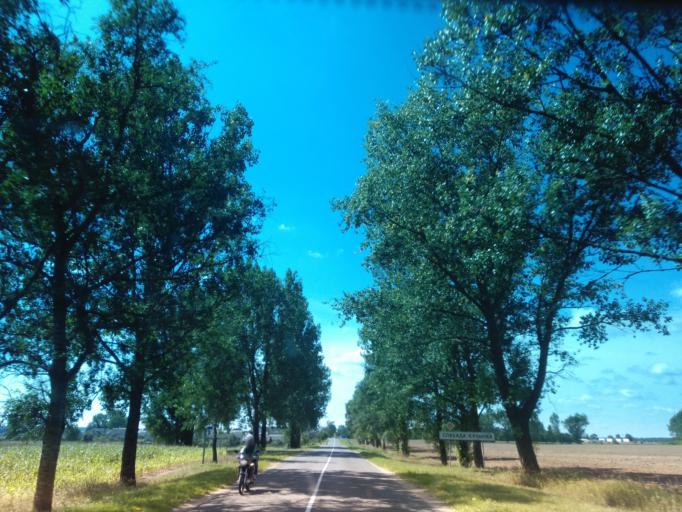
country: BY
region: Minsk
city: Kapyl'
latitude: 53.2630
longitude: 27.1934
